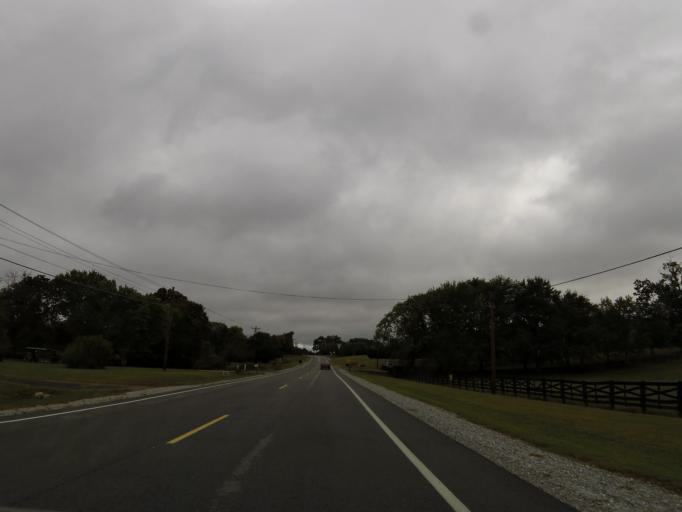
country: US
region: Tennessee
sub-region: Hamilton County
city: Collegedale
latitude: 35.1528
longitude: -85.0399
